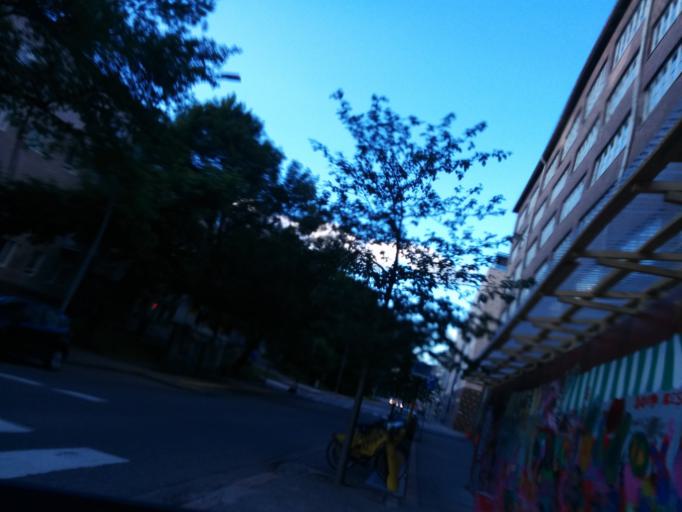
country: FI
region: Uusimaa
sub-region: Helsinki
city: Helsinki
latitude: 60.2099
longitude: 24.9764
